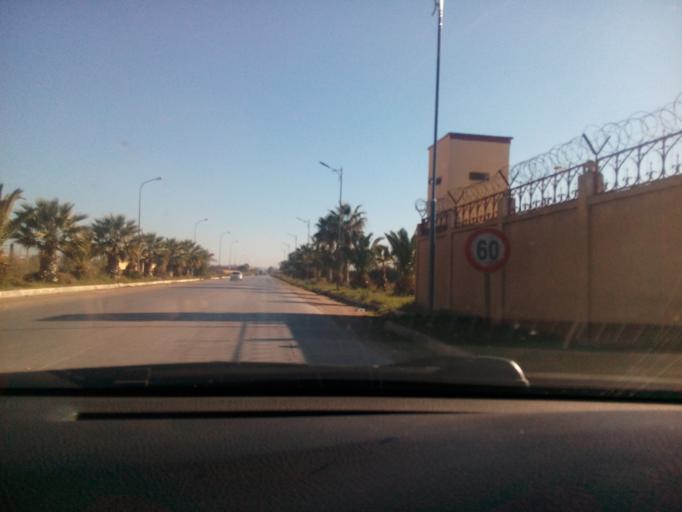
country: DZ
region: Oran
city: Es Senia
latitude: 35.6323
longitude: -0.6045
